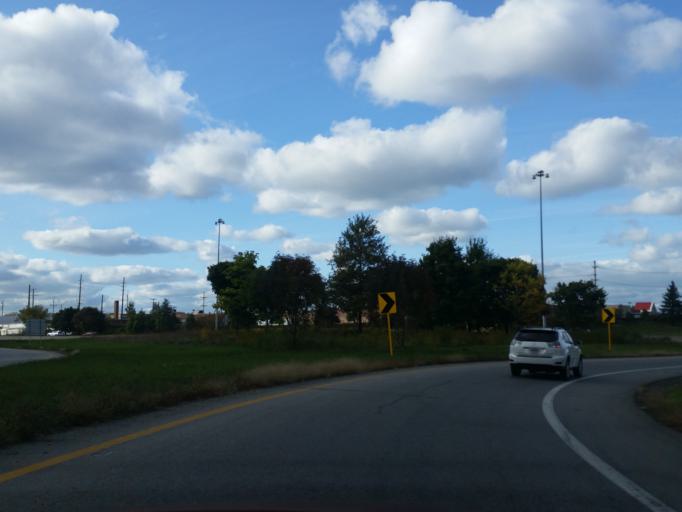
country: US
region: Ohio
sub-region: Cuyahoga County
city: Lakewood
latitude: 41.4654
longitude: -81.7702
